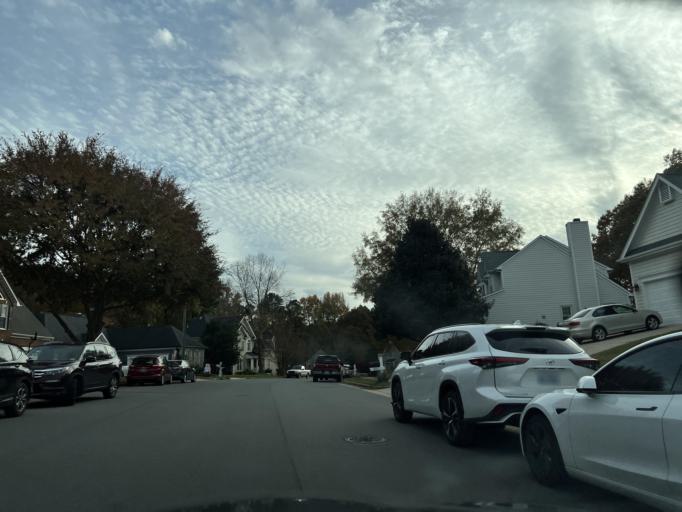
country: US
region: North Carolina
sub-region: Wake County
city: Wake Forest
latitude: 35.8939
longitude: -78.5903
